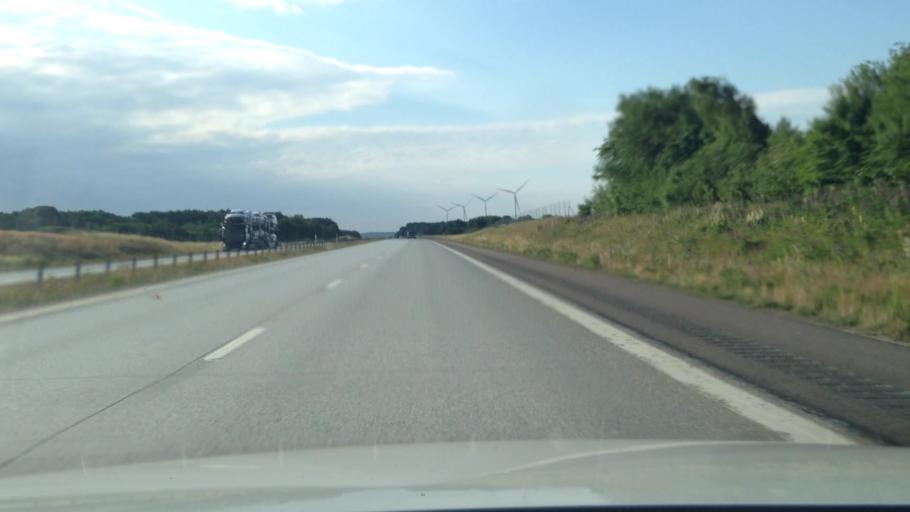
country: SE
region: Halland
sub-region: Falkenbergs Kommun
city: Falkenberg
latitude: 56.9644
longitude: 12.4465
